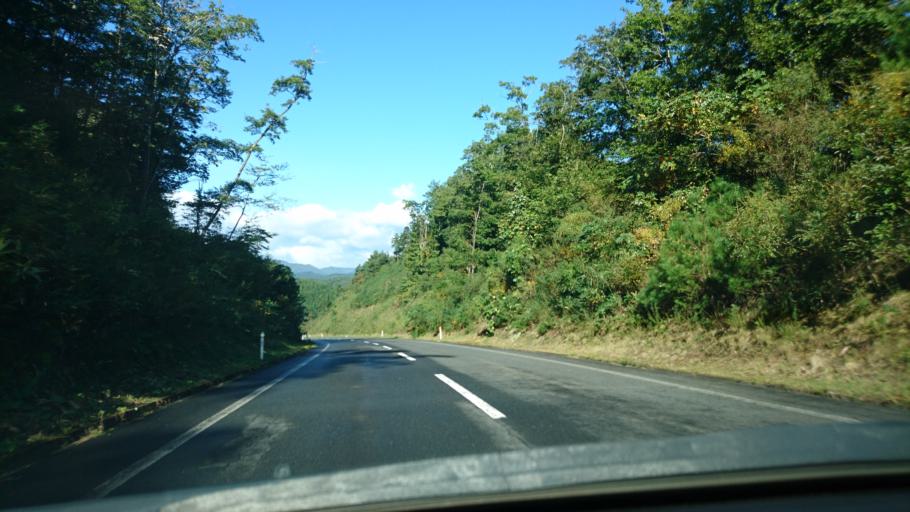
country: JP
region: Iwate
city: Ichinoseki
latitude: 39.0052
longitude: 141.0368
